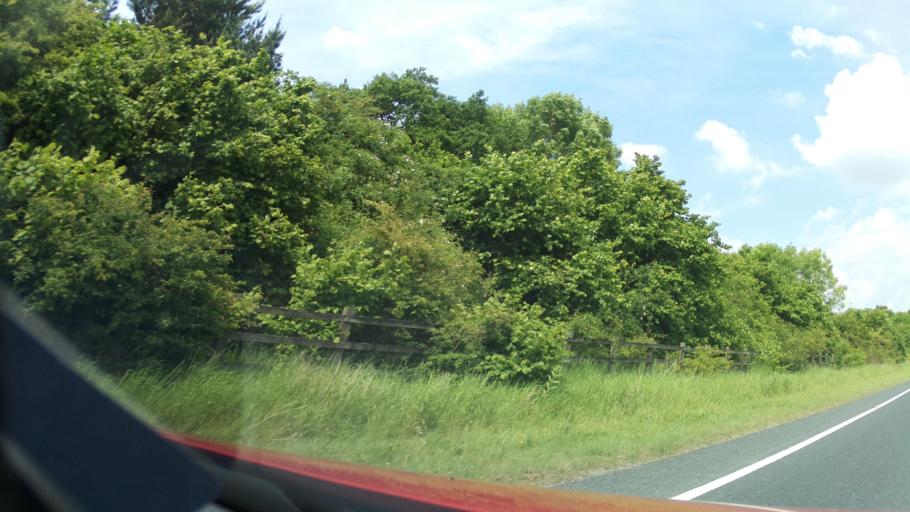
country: GB
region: England
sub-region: North Yorkshire
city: Boroughbridge
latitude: 54.0568
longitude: -1.3886
